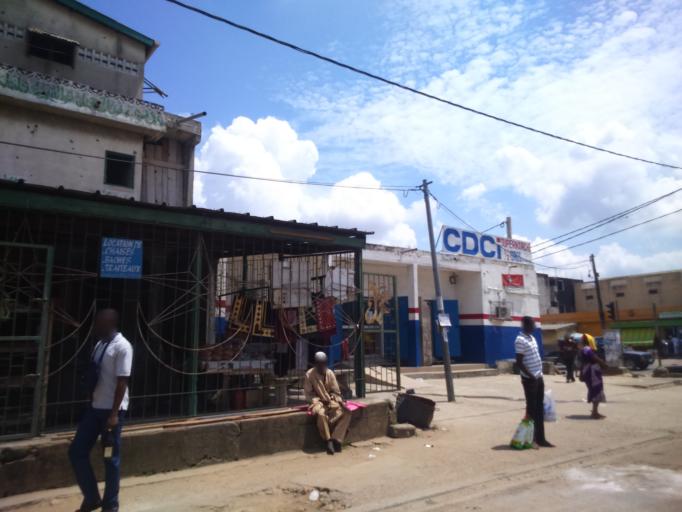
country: CI
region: Lagunes
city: Abidjan
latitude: 5.3467
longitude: -4.0875
